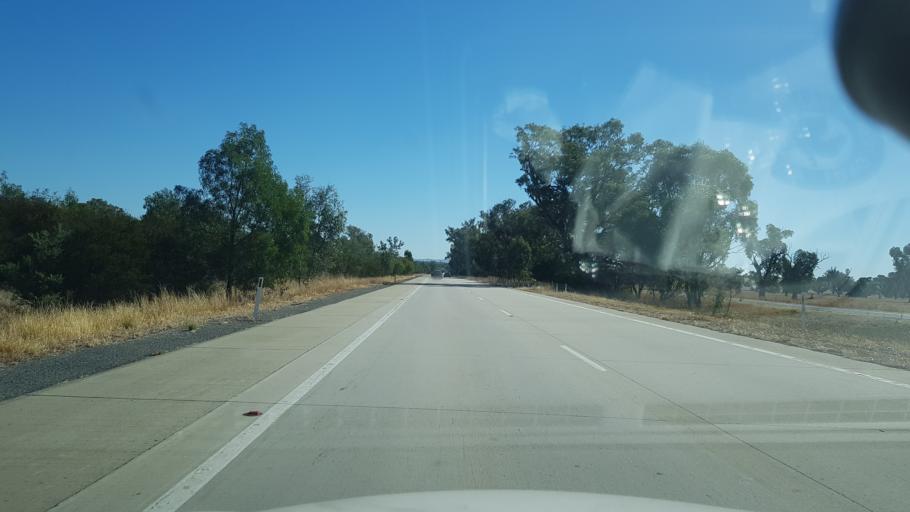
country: AU
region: New South Wales
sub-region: Greater Hume Shire
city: Jindera
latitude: -35.9248
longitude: 147.0424
